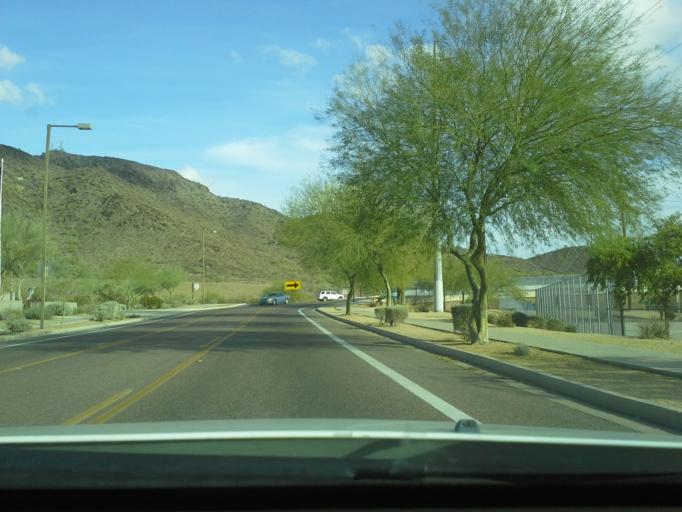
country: US
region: Arizona
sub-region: Maricopa County
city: Glendale
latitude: 33.5822
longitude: -112.0839
